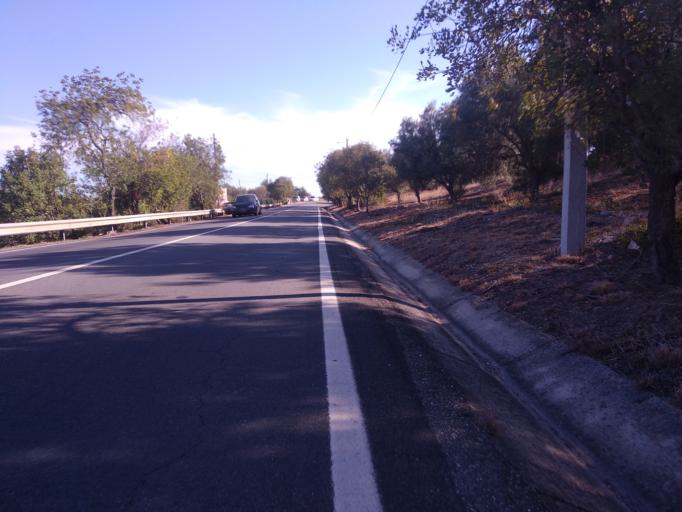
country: PT
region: Faro
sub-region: Sao Bras de Alportel
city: Sao Bras de Alportel
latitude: 37.1031
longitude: -7.9045
